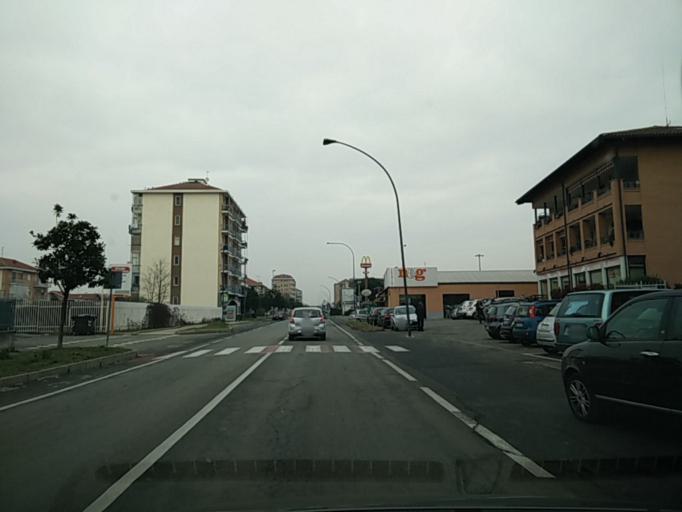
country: IT
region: Piedmont
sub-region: Provincia di Torino
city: Leini
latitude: 45.1641
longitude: 7.7114
